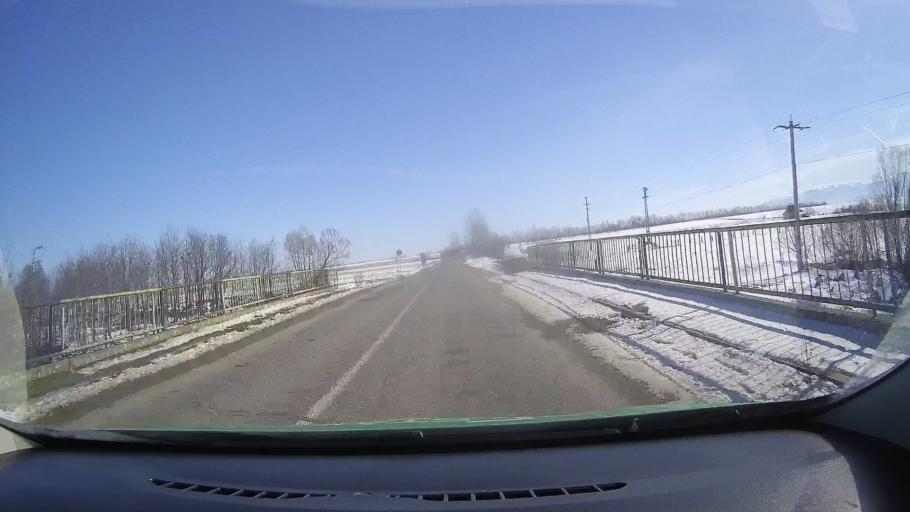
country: RO
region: Brasov
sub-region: Comuna Dragus
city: Dragus
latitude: 45.7531
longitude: 24.7439
